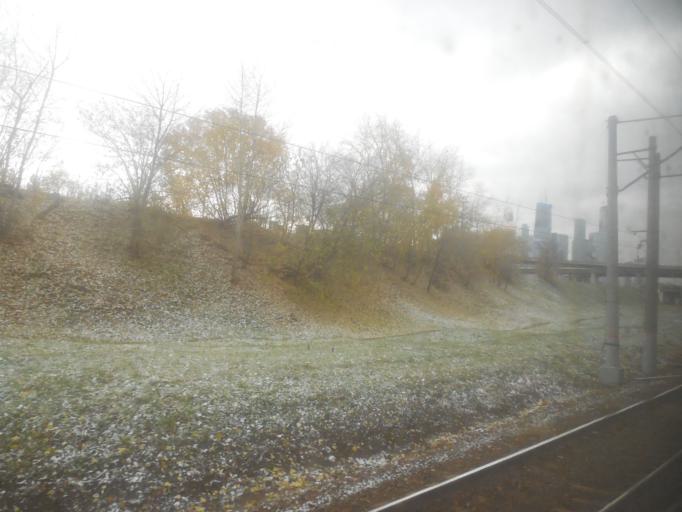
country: RU
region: Moskovskaya
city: Presnenskiy
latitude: 55.7690
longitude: 37.5369
